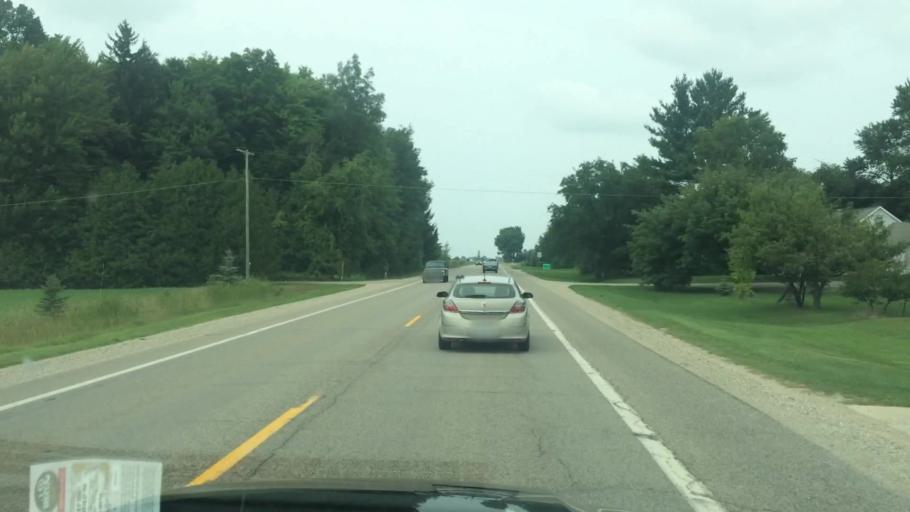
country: US
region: Michigan
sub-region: Huron County
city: Bad Axe
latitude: 43.9002
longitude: -83.0035
